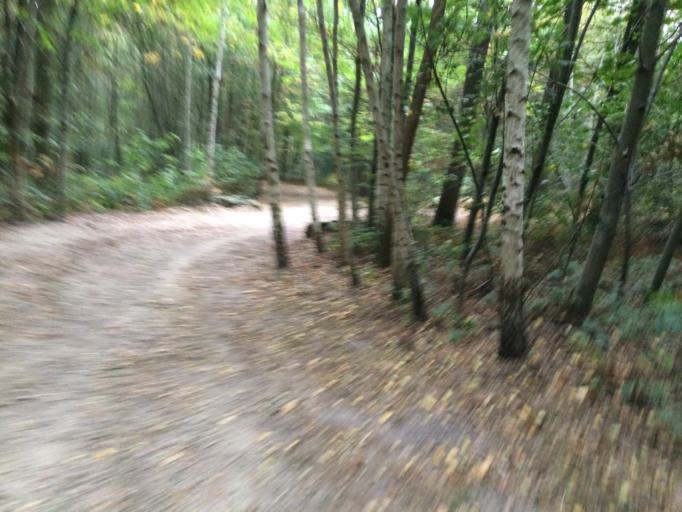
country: FR
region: Ile-de-France
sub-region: Departement de l'Essonne
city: Orsay
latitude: 48.6964
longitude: 2.2044
